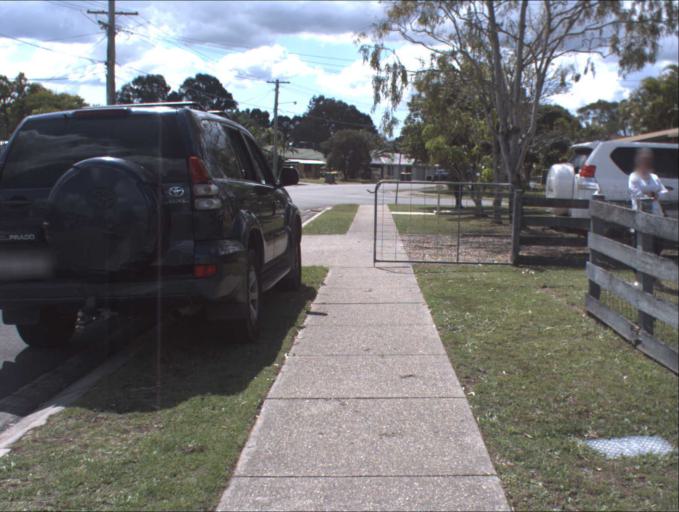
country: AU
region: Queensland
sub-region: Logan
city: Waterford West
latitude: -27.6817
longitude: 153.1476
